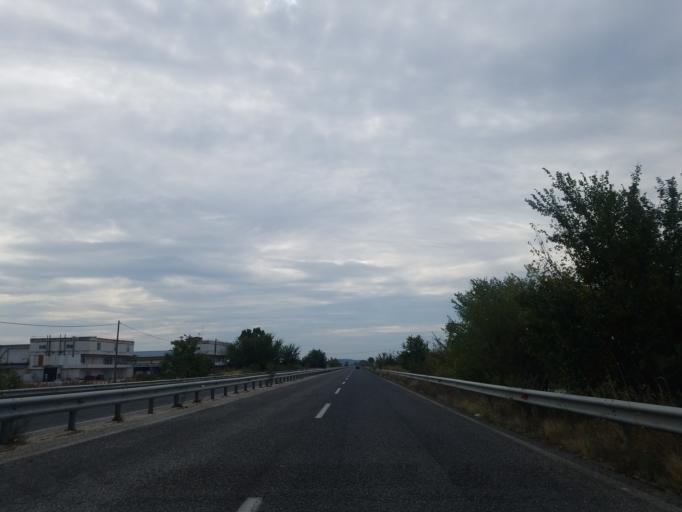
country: GR
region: Thessaly
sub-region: Trikala
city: Vasiliki
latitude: 39.6134
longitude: 21.7188
